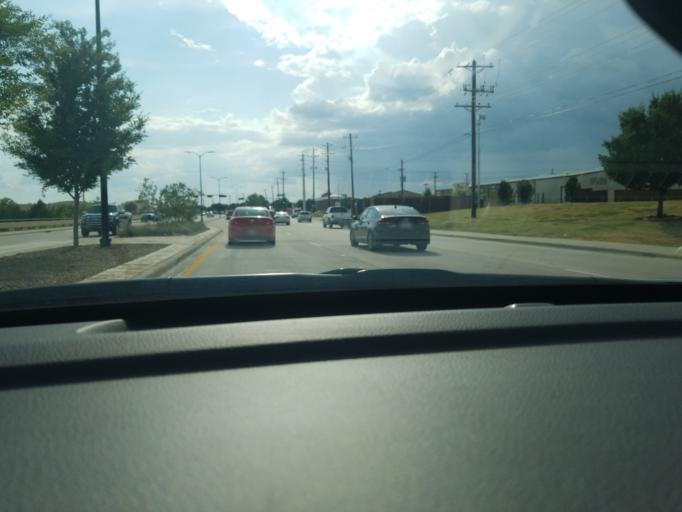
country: US
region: Texas
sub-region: Denton County
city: Little Elm
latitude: 33.1691
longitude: -96.9204
